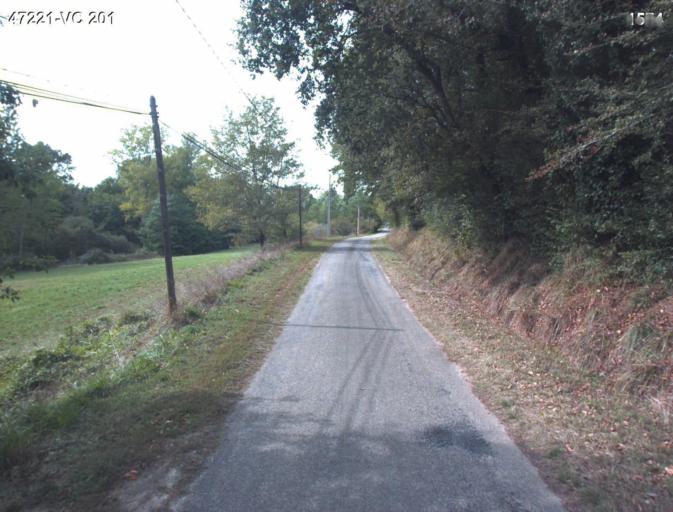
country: FR
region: Aquitaine
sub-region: Departement du Lot-et-Garonne
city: Mezin
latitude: 44.1113
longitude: 0.2379
